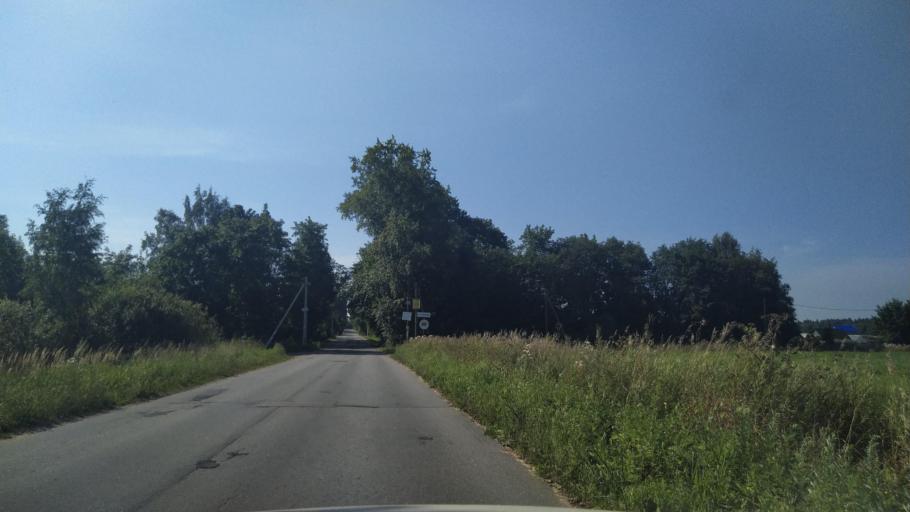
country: RU
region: Leningrad
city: Siverskiy
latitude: 59.2786
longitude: 30.0499
